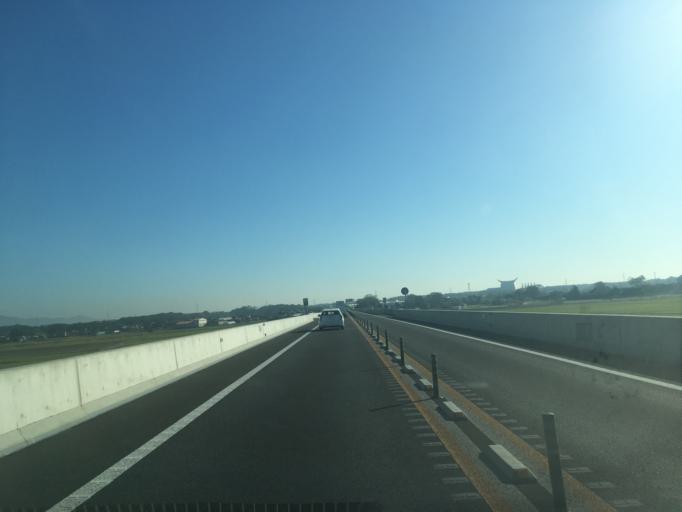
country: JP
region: Ibaraki
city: Ishige
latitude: 36.0791
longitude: 139.9916
